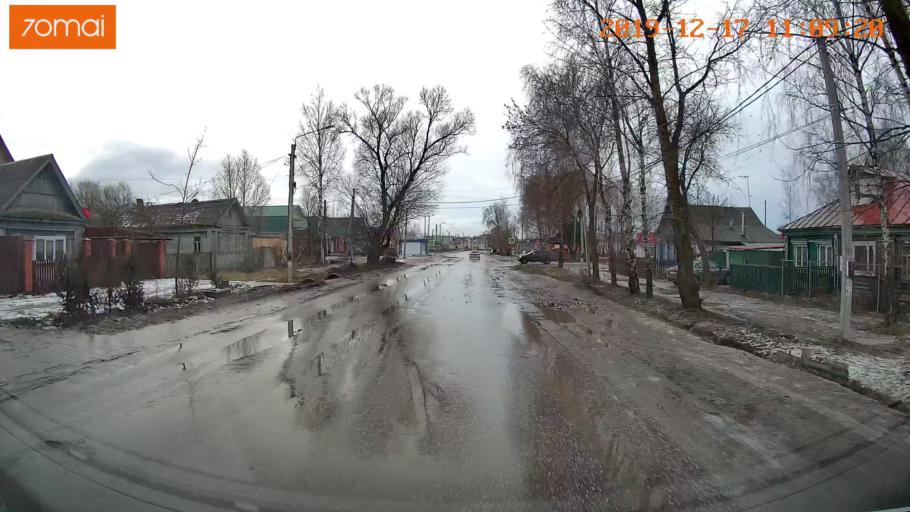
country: RU
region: Vladimir
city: Gus'-Khrustal'nyy
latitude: 55.6013
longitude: 40.6425
